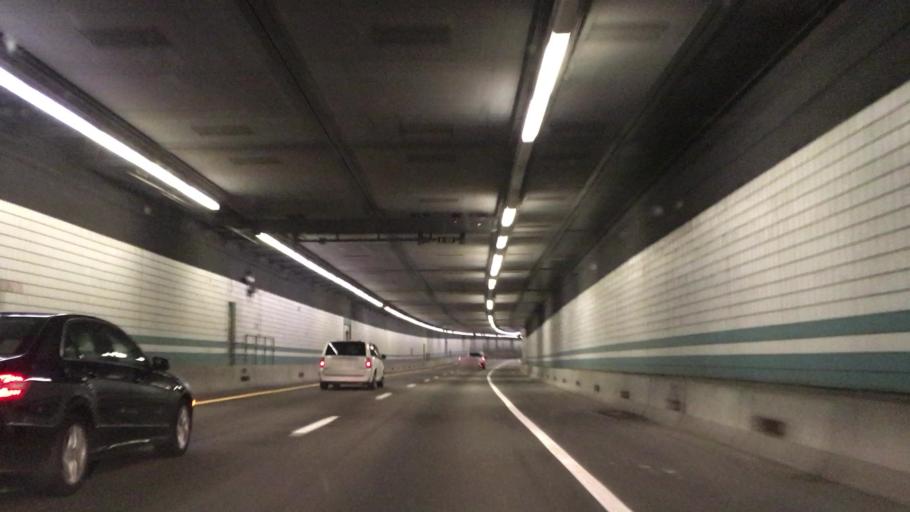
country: US
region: Massachusetts
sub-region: Suffolk County
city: South Boston
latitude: 42.3454
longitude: -71.0509
